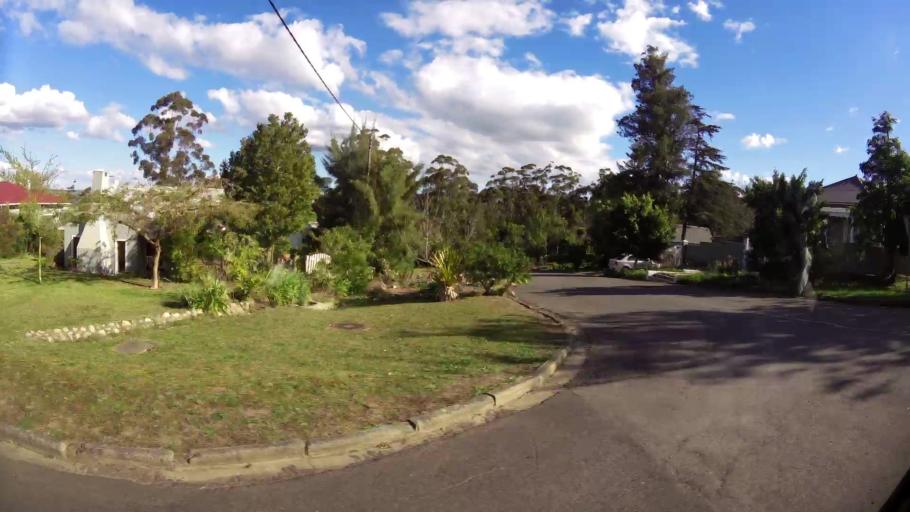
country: ZA
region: Western Cape
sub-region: Overberg District Municipality
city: Swellendam
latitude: -34.0187
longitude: 20.4373
